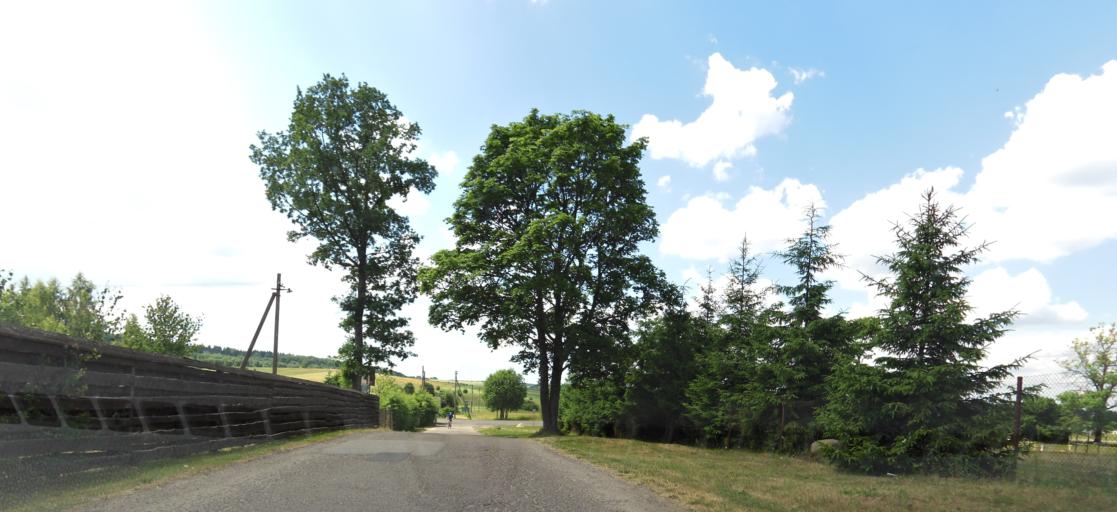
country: LT
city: Skaidiskes
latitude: 54.5377
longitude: 25.6470
